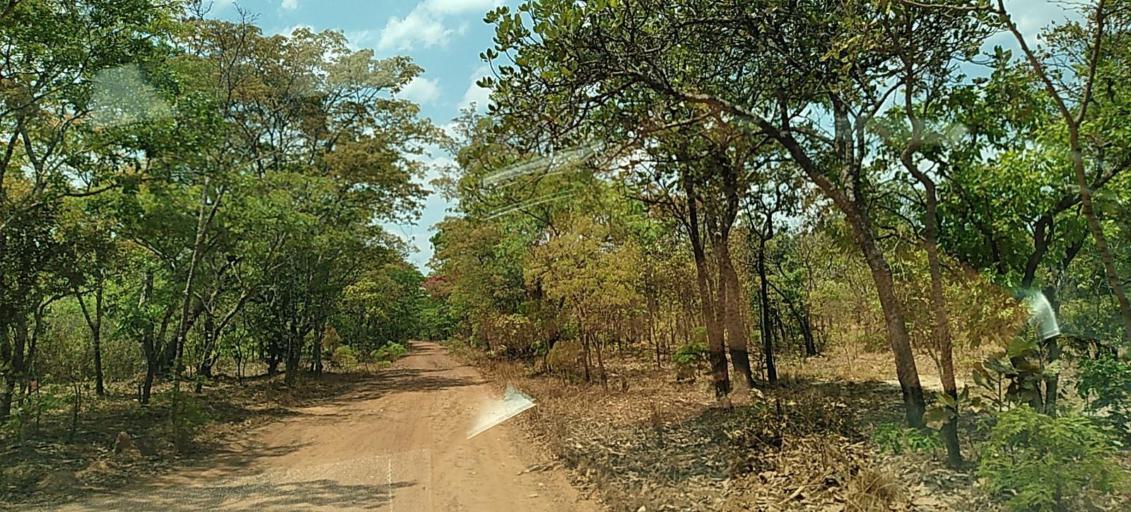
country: ZM
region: Copperbelt
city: Chililabombwe
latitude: -12.5117
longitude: 27.6299
